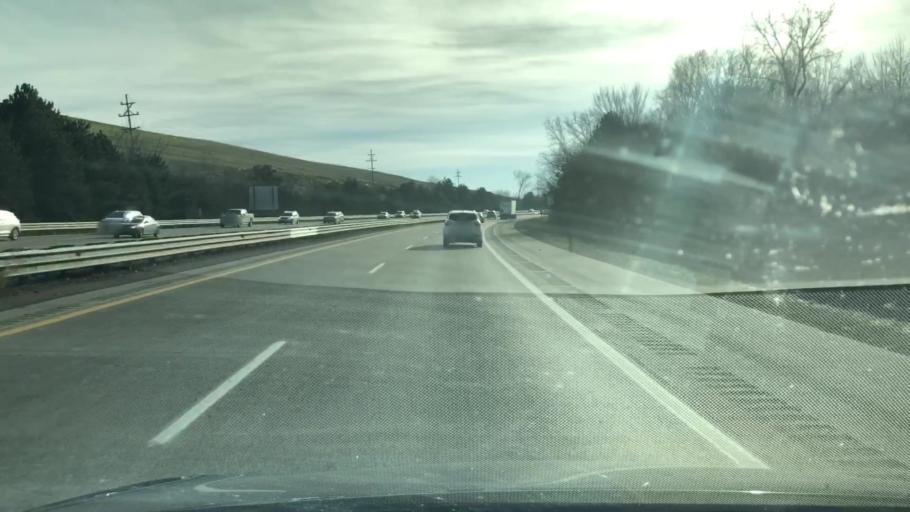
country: US
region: Michigan
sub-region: Genesee County
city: Lake Fenton
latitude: 42.9074
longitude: -83.7268
